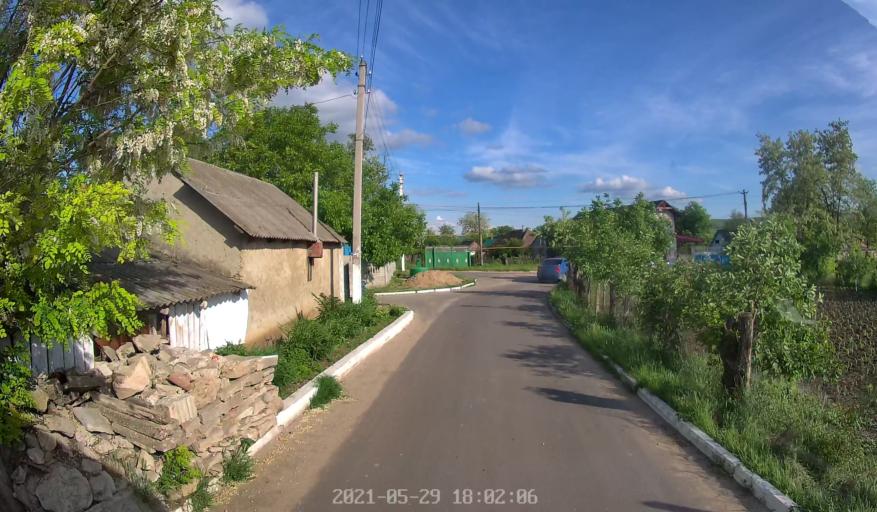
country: MD
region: Laloveni
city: Ialoveni
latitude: 46.8360
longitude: 28.8511
